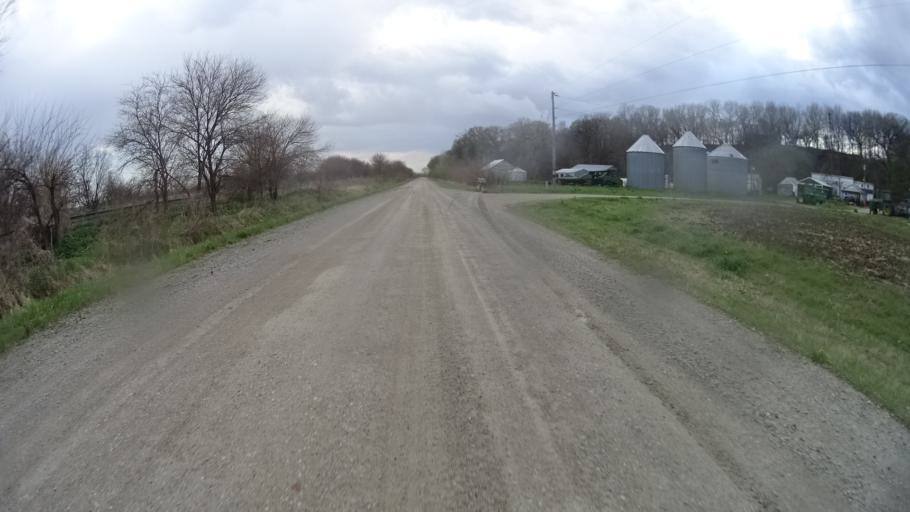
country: US
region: Nebraska
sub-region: Sarpy County
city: Offutt Air Force Base
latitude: 41.0884
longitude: -95.9154
